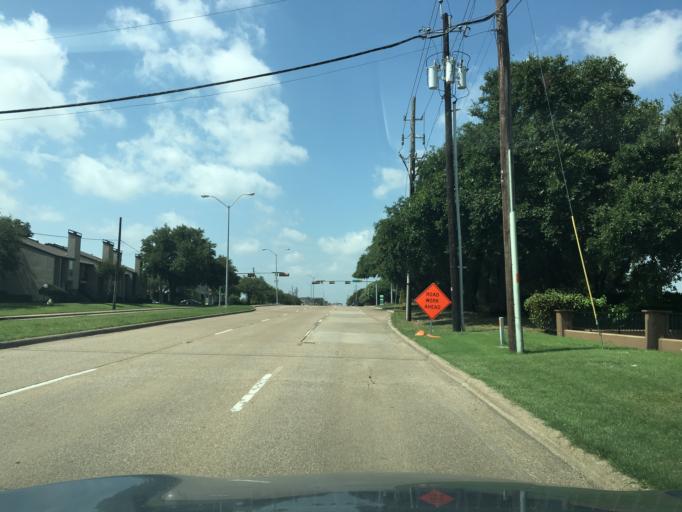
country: US
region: Texas
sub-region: Dallas County
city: Richardson
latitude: 32.9208
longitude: -96.7416
